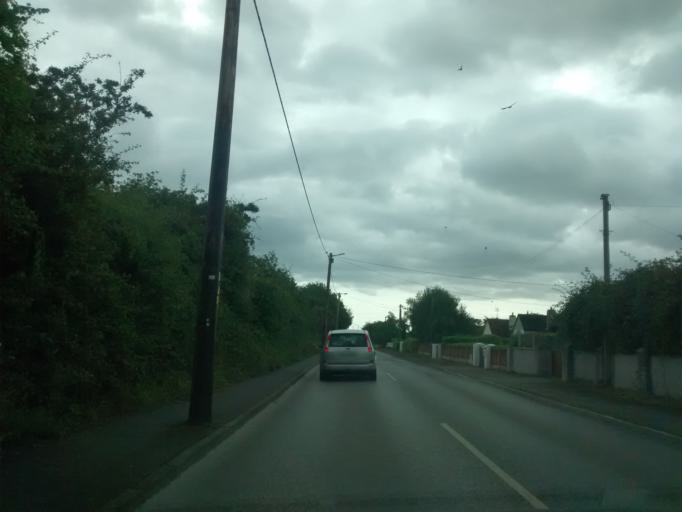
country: IE
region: Leinster
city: Portraine
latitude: 53.4795
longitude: -6.1240
